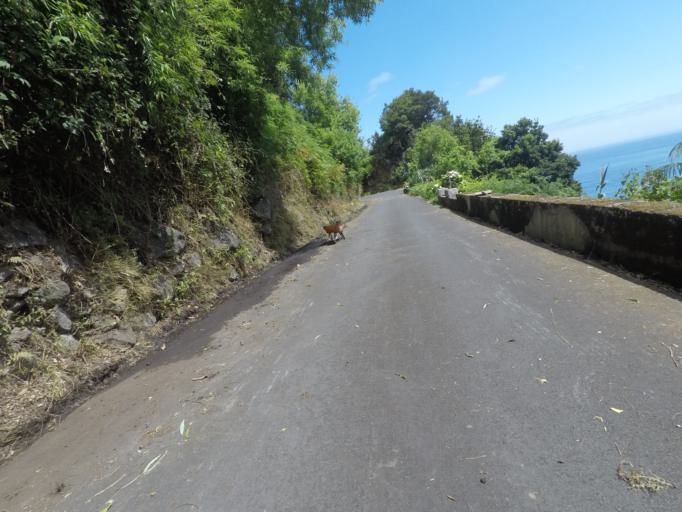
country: PT
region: Madeira
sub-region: Sao Vicente
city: Sao Vicente
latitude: 32.8160
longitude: -17.0995
